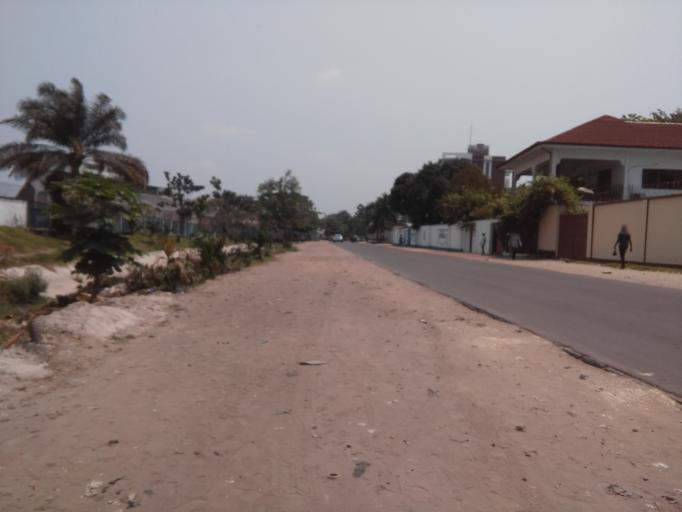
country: CD
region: Kinshasa
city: Kinshasa
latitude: -4.3173
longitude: 15.2908
